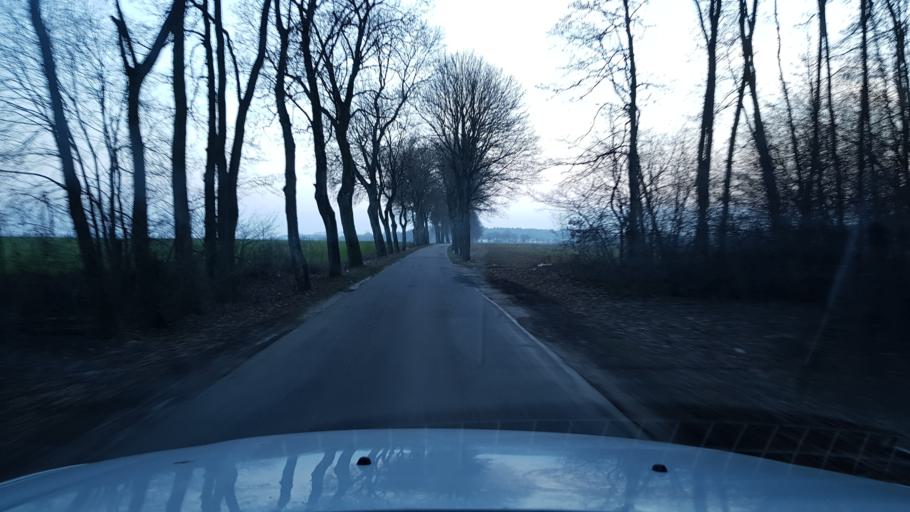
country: PL
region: West Pomeranian Voivodeship
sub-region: Powiat bialogardzki
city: Karlino
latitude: 54.0034
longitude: 15.8306
